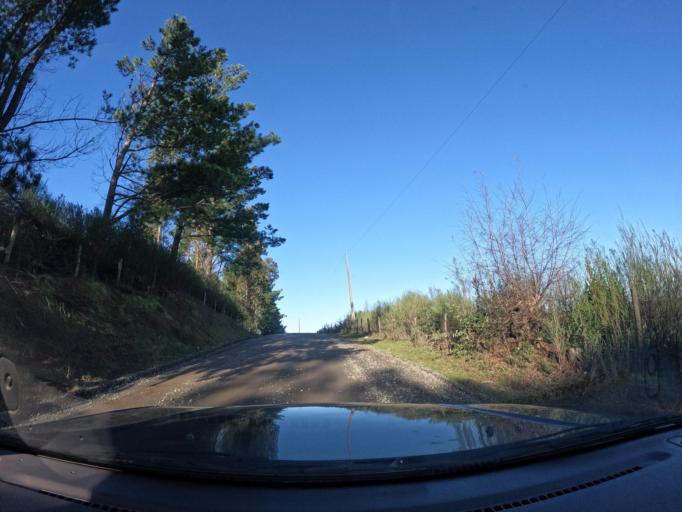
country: CL
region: Biobio
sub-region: Provincia de Concepcion
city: Chiguayante
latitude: -37.0124
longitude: -72.8661
